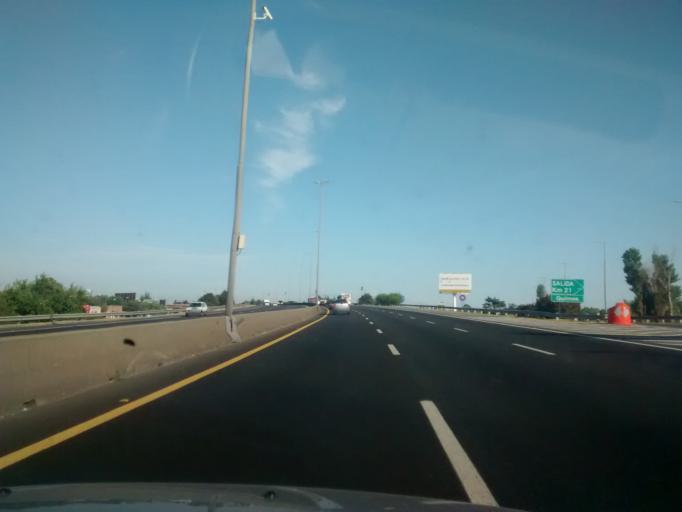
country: AR
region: Buenos Aires
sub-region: Partido de Quilmes
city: Quilmes
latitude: -34.7185
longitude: -58.2324
